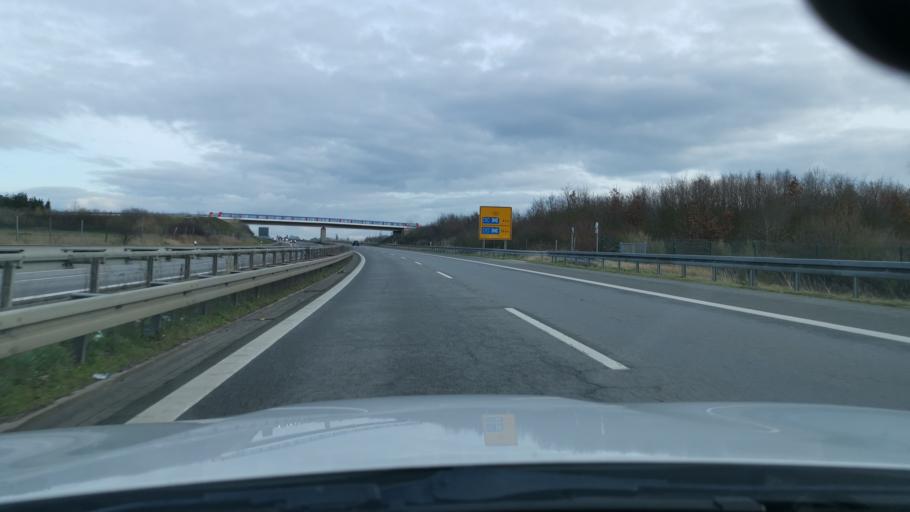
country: DE
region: Mecklenburg-Vorpommern
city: Stabelow
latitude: 54.0406
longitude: 12.0396
